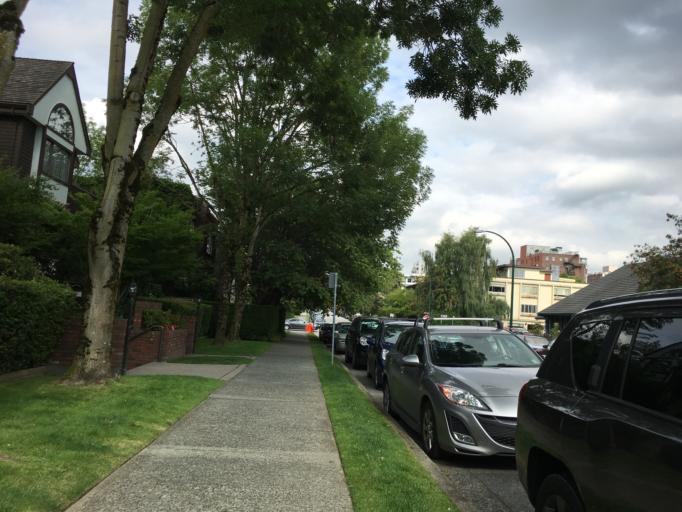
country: CA
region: British Columbia
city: West End
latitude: 49.2618
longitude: -123.1422
